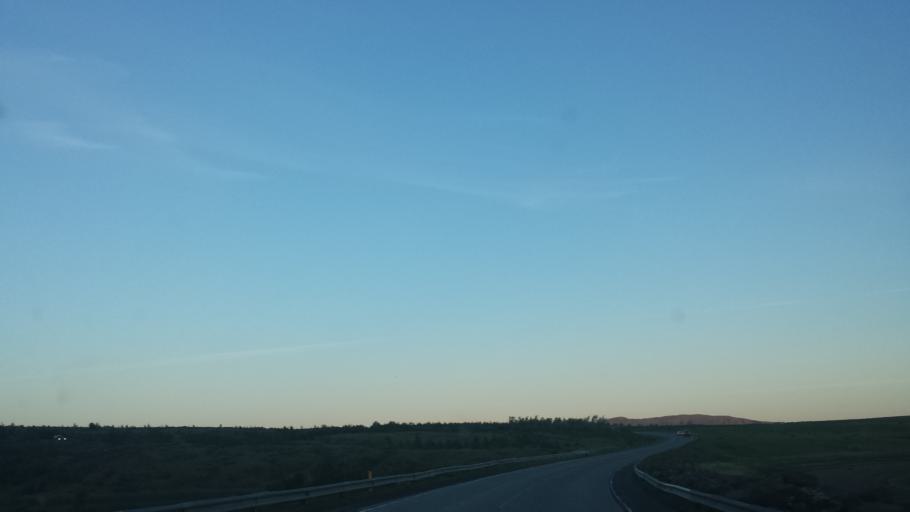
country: IS
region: Capital Region
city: Mosfellsbaer
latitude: 64.2042
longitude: -21.7079
